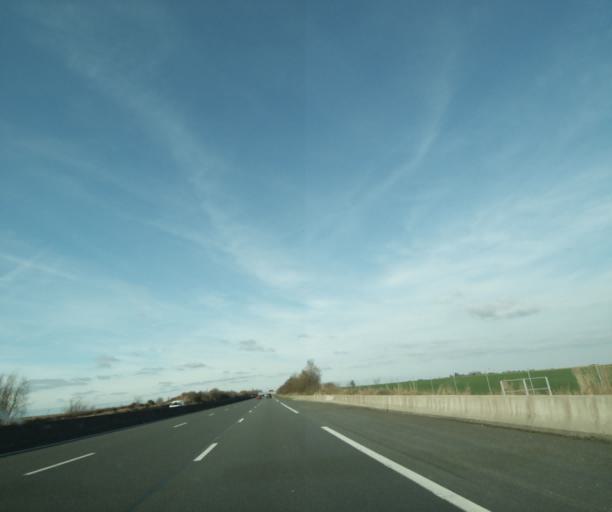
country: FR
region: Centre
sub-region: Departement d'Eure-et-Loir
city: Aunay-sous-Auneau
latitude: 48.4218
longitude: 1.9002
